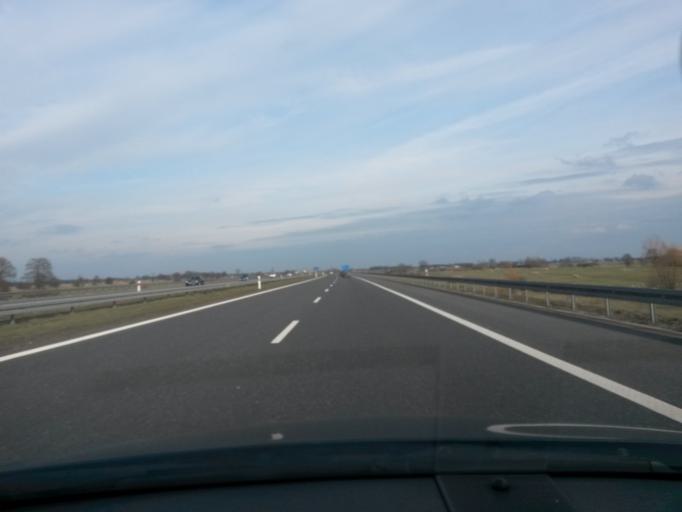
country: PL
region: Lodz Voivodeship
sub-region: Powiat poddebicki
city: Wartkowice
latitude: 52.0001
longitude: 19.0043
